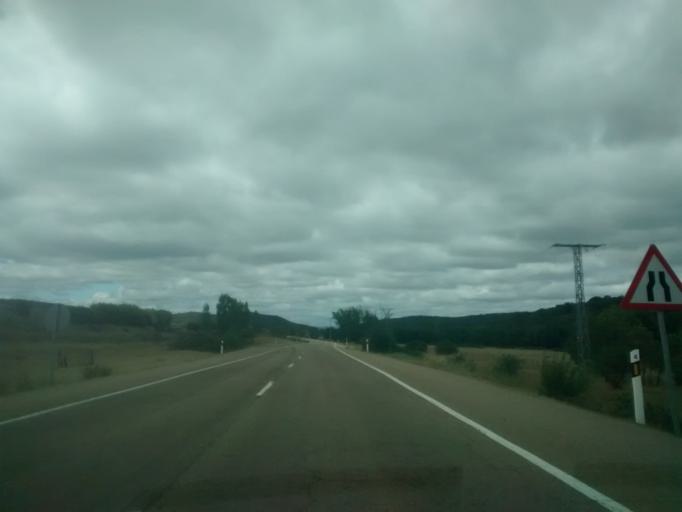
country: ES
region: Castille and Leon
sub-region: Provincia de Salamanca
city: Ciudad Rodrigo
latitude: 40.6474
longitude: -6.4643
